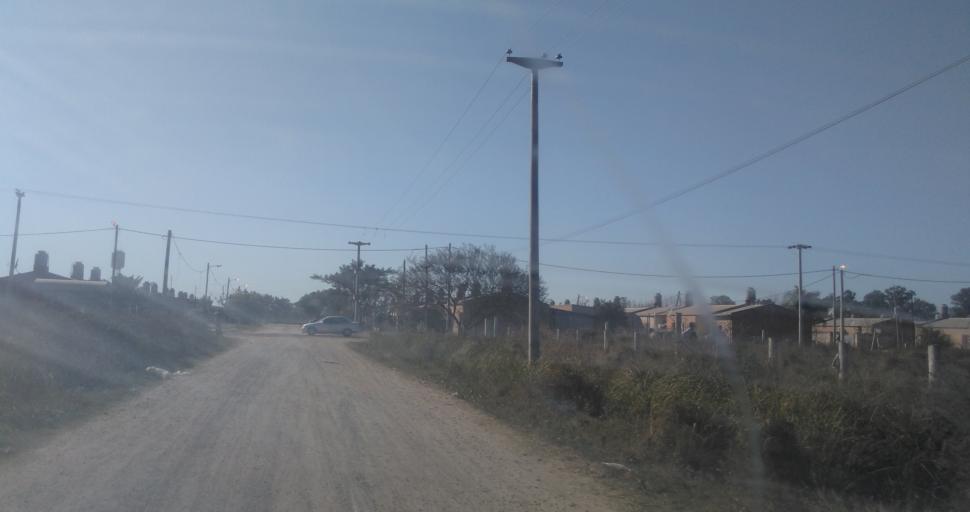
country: AR
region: Chaco
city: Fontana
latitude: -27.4577
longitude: -59.0455
